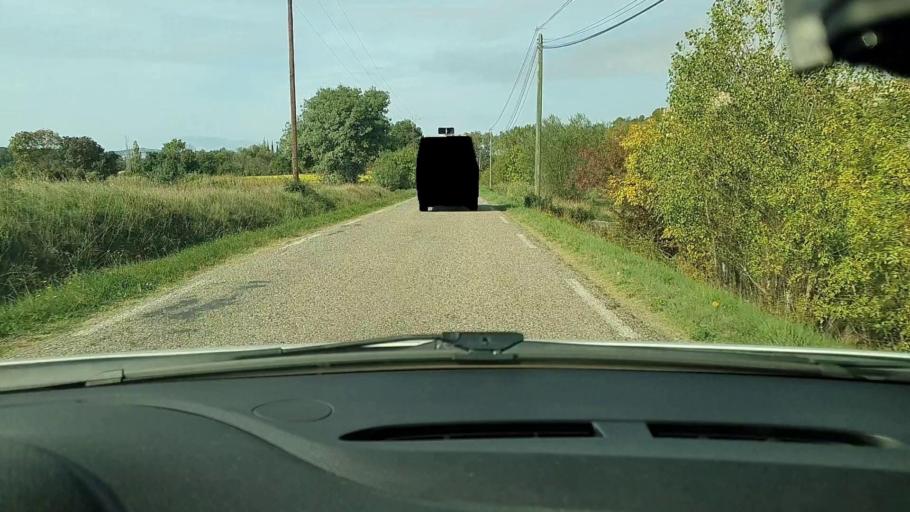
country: FR
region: Languedoc-Roussillon
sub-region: Departement du Gard
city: Goudargues
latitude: 44.1497
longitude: 4.3727
